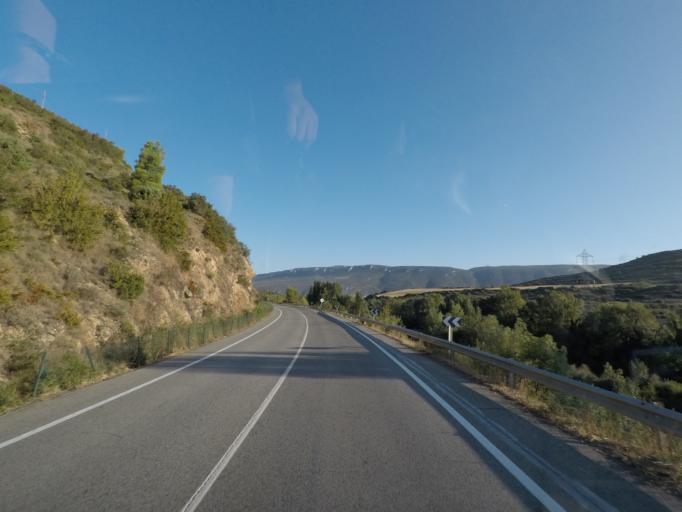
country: ES
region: Navarre
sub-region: Provincia de Navarra
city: Liedena
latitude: 42.6010
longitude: -1.2759
